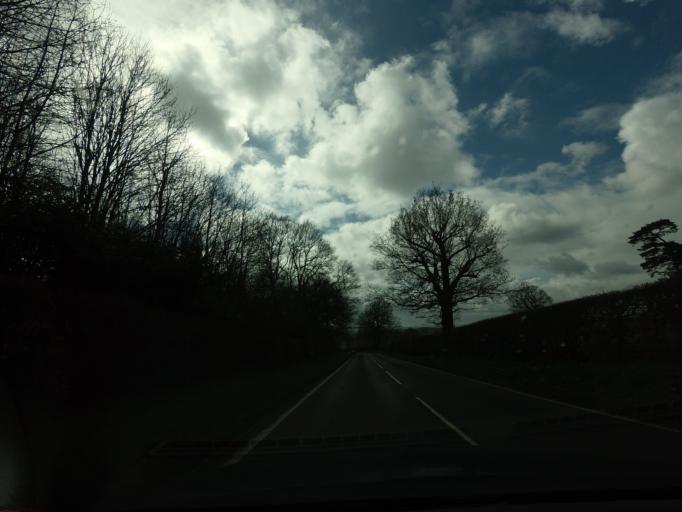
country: GB
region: England
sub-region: Kent
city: Borough Green
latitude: 51.2605
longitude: 0.2821
